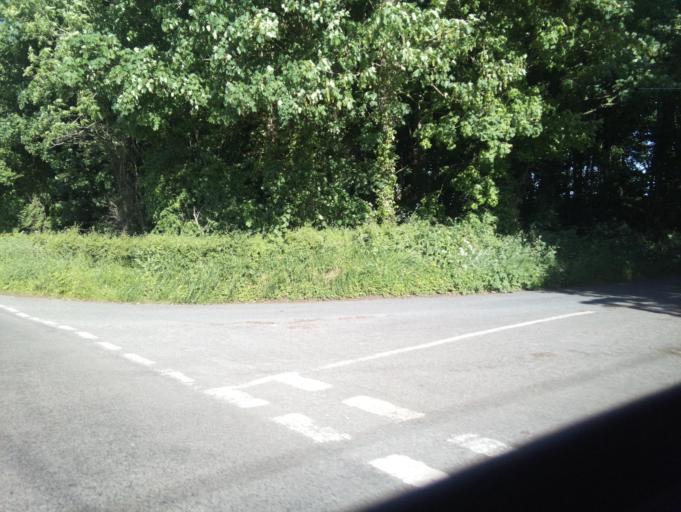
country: GB
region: England
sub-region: Dorset
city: Sherborne
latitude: 50.9427
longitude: -2.5427
